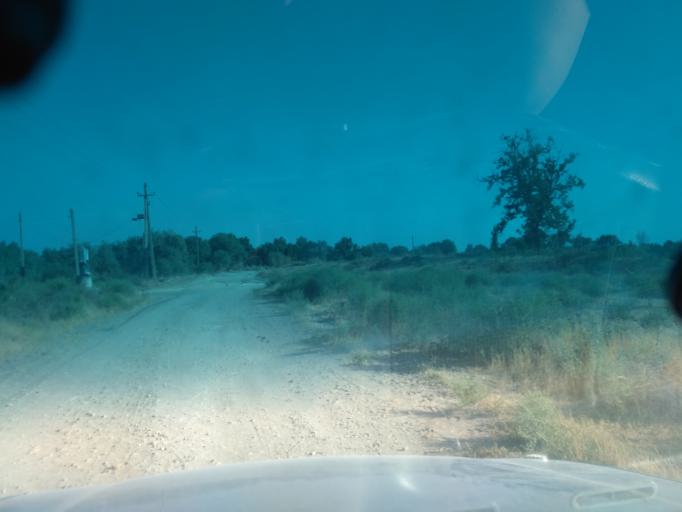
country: TJ
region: Viloyati Sughd
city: Buston
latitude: 40.5573
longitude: 69.0752
